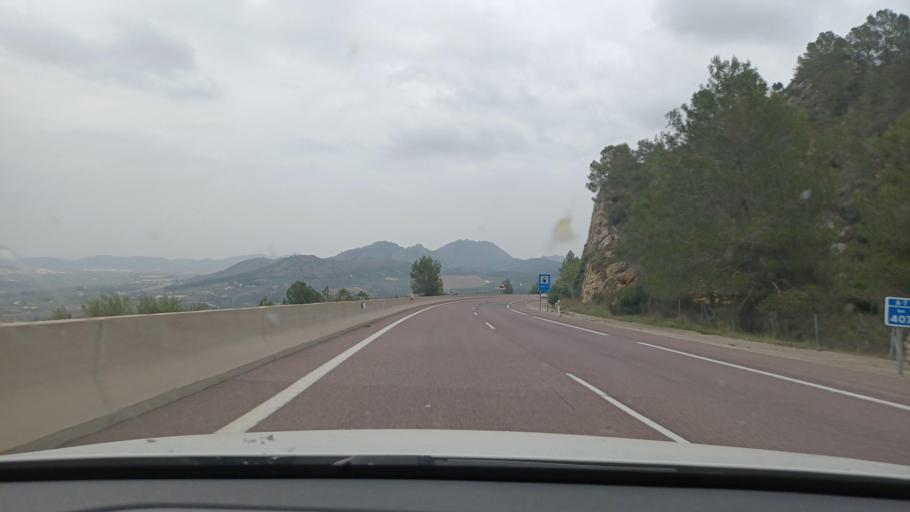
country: ES
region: Valencia
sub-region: Provincia de Valencia
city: L'Olleria
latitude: 38.9360
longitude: -0.5708
